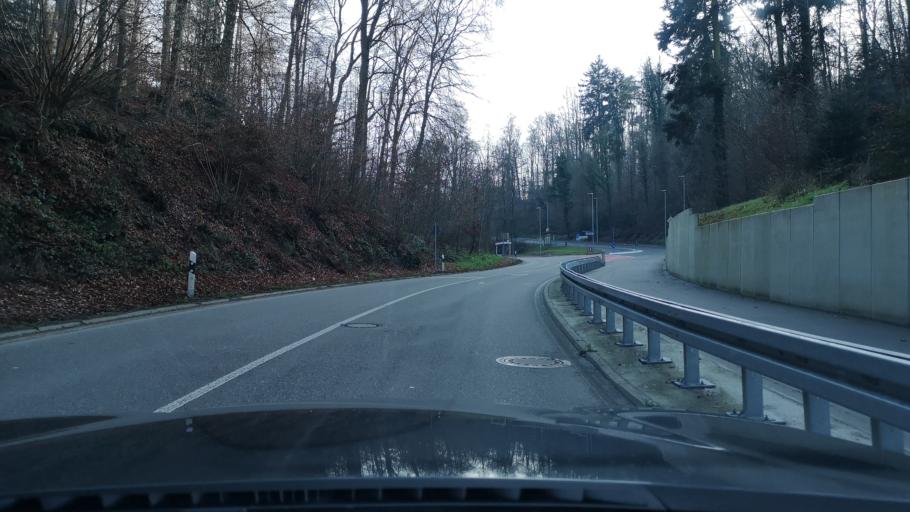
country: DE
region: Baden-Wuerttemberg
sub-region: Karlsruhe Region
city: Ettlingen
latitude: 48.9743
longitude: 8.4729
